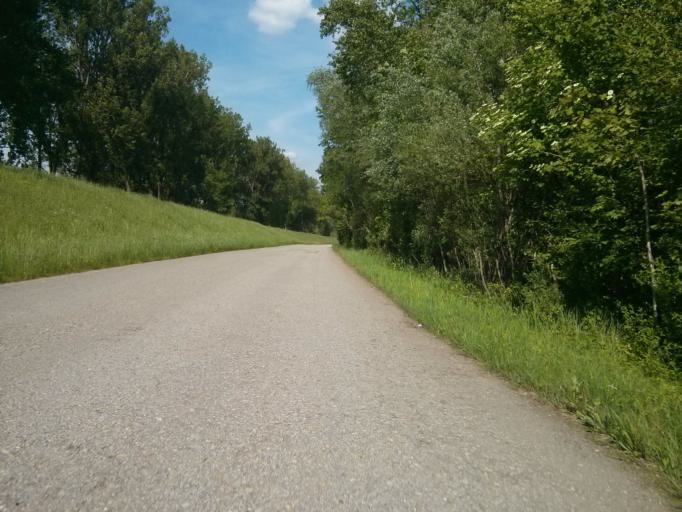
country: DE
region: Bavaria
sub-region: Lower Bavaria
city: Plattling
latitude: 48.7642
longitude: 12.8743
